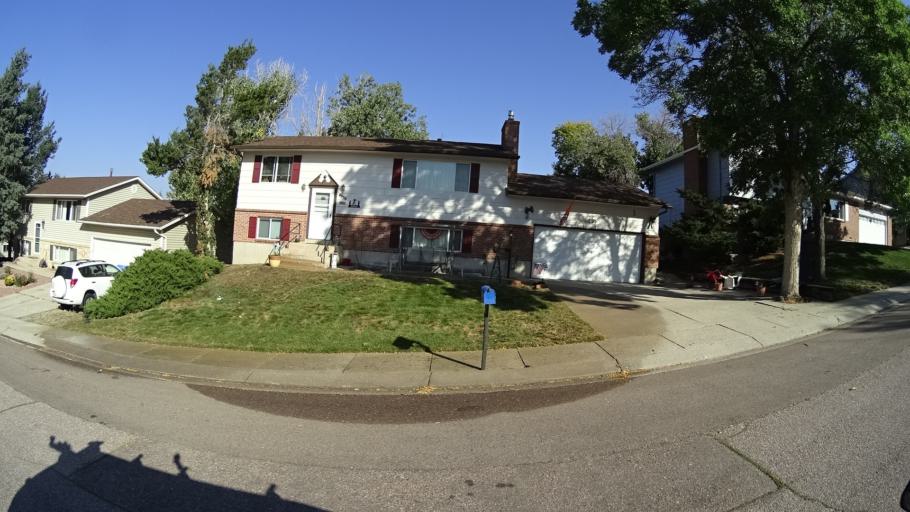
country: US
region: Colorado
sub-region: El Paso County
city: Cimarron Hills
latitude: 38.8796
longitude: -104.7353
